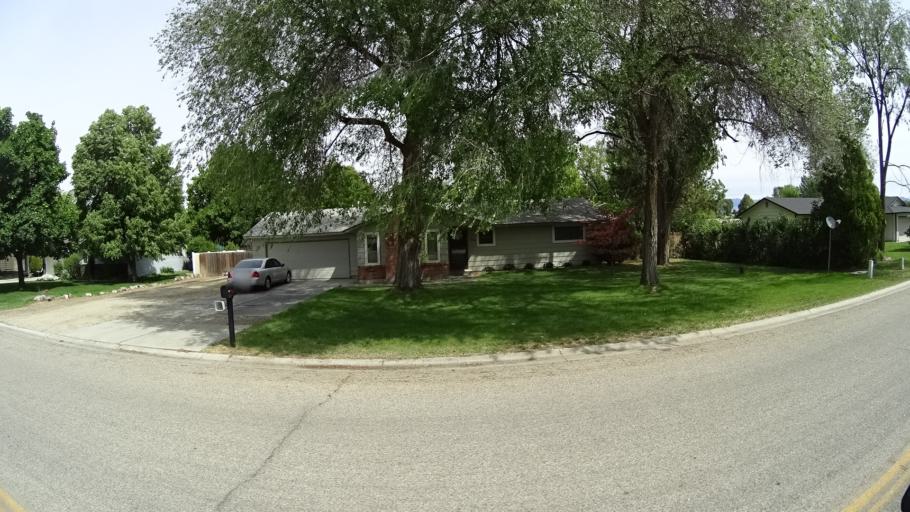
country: US
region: Idaho
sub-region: Ada County
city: Meridian
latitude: 43.5539
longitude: -116.3308
